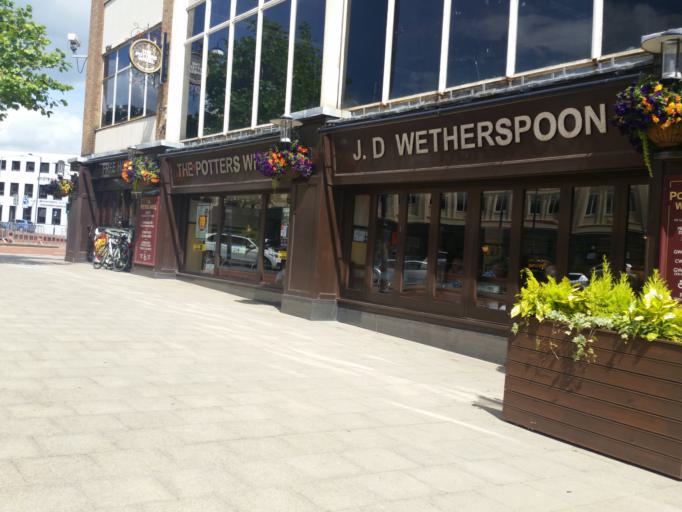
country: GB
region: Wales
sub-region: City and County of Swansea
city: Swansea
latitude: 51.6193
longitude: -3.9496
